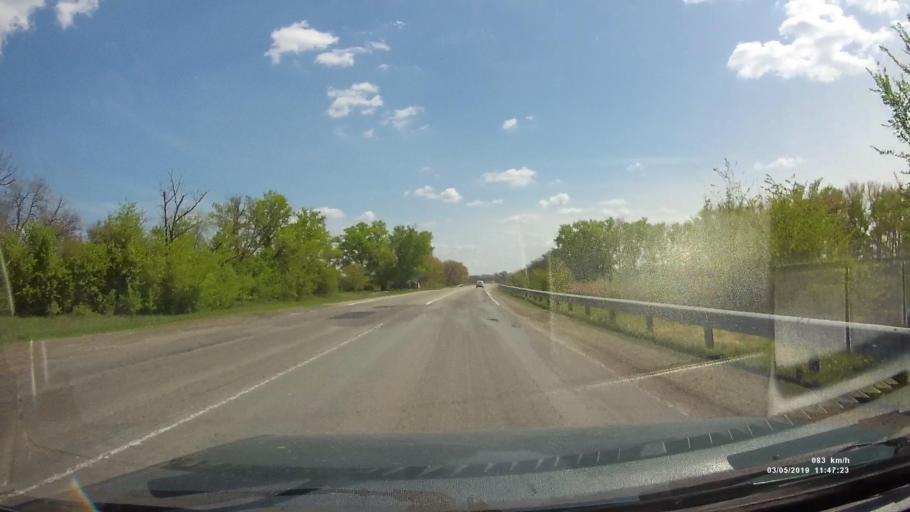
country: RU
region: Rostov
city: Starocherkasskaya
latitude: 47.1512
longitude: 40.1392
